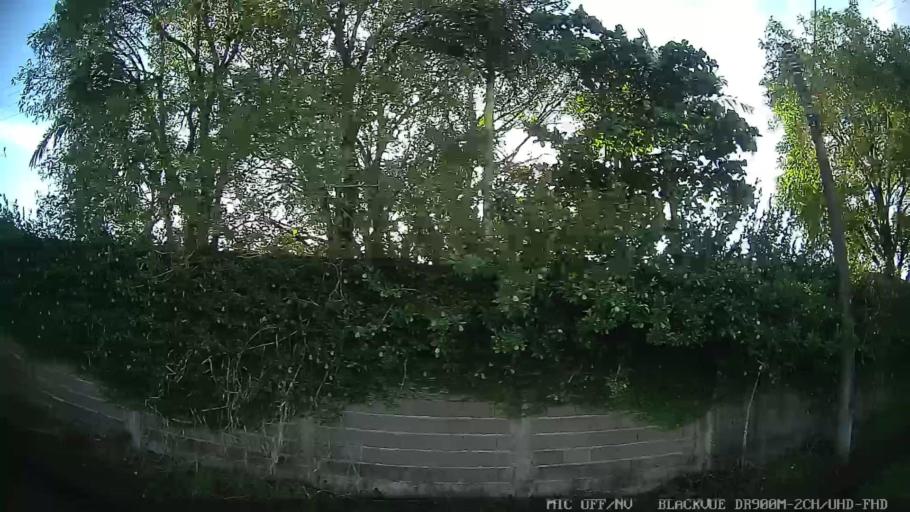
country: BR
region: Sao Paulo
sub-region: Iguape
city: Iguape
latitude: -24.7556
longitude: -47.5678
